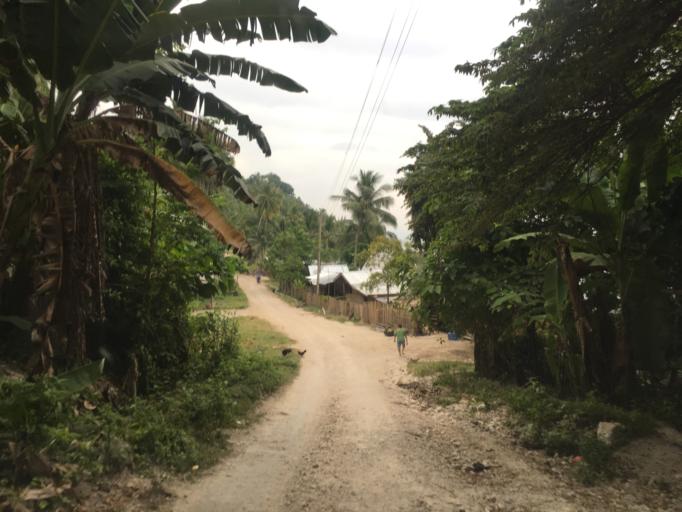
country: PH
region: Davao
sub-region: Province of Davao del Norte
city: San Remigio
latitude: 6.9404
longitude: 125.7919
